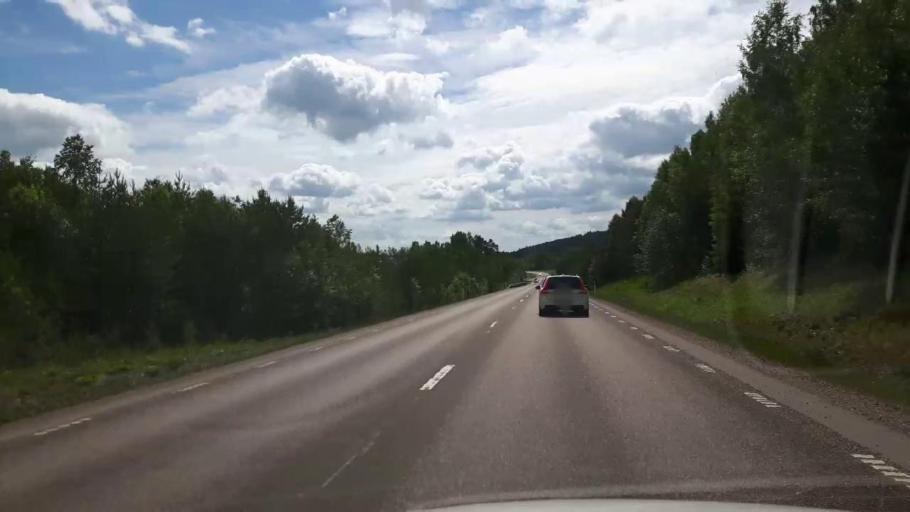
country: SE
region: Dalarna
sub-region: Saters Kommun
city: Saeter
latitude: 60.4538
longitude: 15.8062
